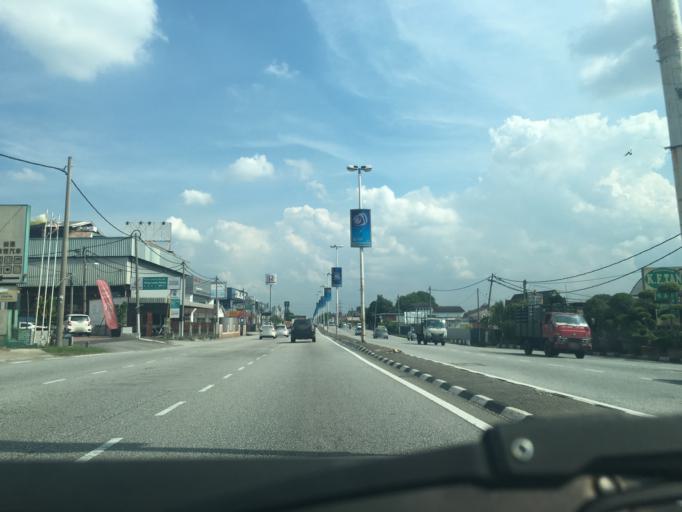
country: MY
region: Perak
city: Ipoh
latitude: 4.6269
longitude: 101.0821
